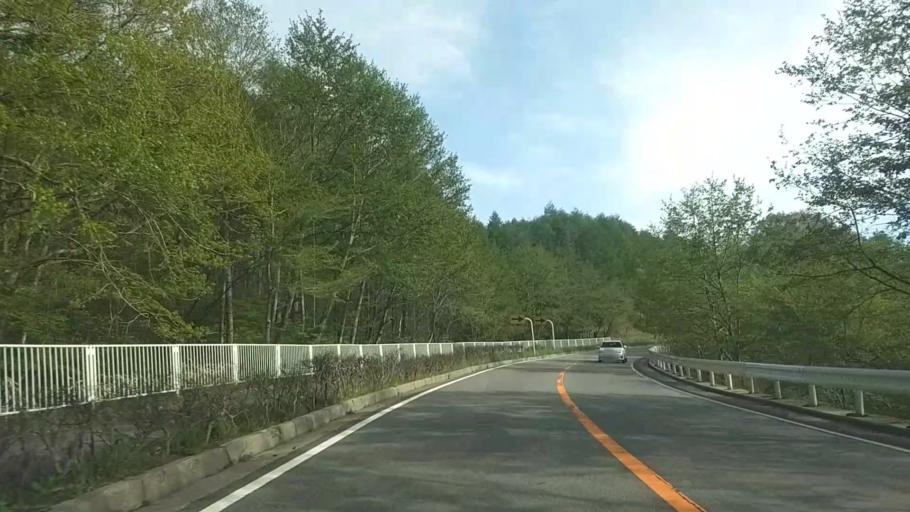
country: JP
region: Yamanashi
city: Nirasaki
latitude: 35.9334
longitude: 138.4472
